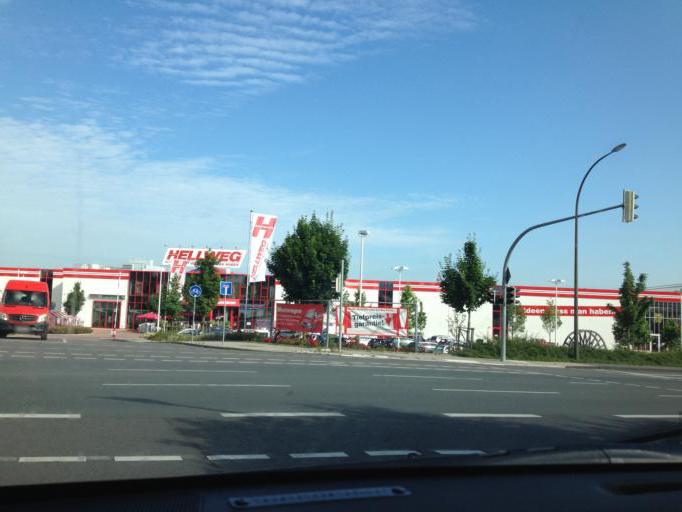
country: DE
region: North Rhine-Westphalia
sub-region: Regierungsbezirk Arnsberg
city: Dortmund
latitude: 51.4724
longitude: 7.4860
